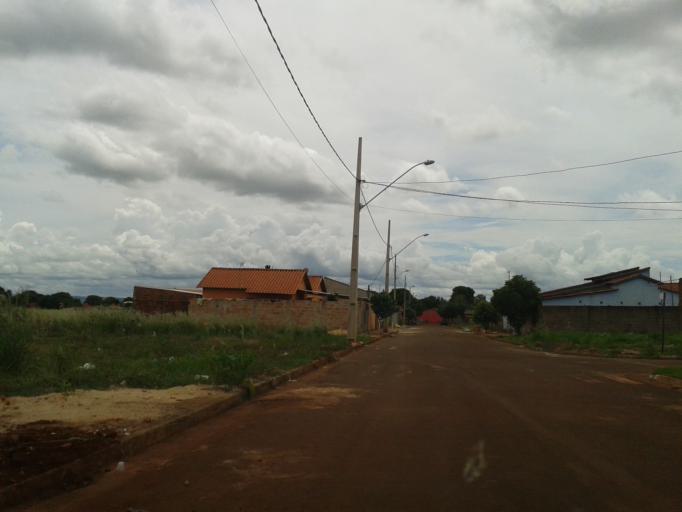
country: BR
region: Minas Gerais
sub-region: Centralina
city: Centralina
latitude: -18.5861
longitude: -49.2058
